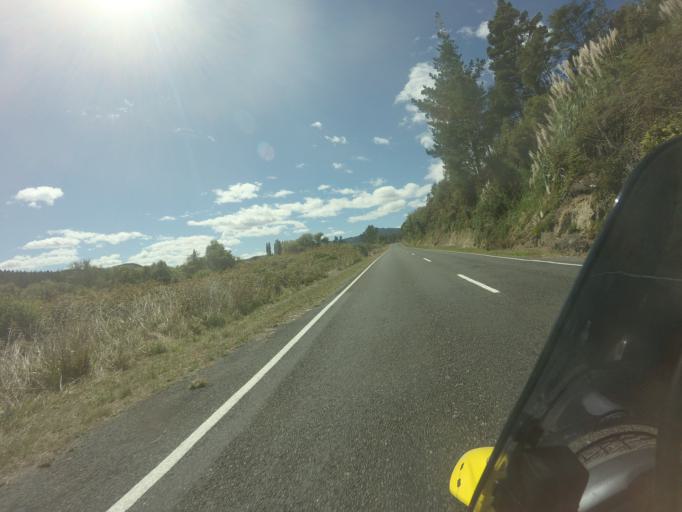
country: NZ
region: Bay of Plenty
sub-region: Kawerau District
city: Kawerau
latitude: -38.2517
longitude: 176.8225
